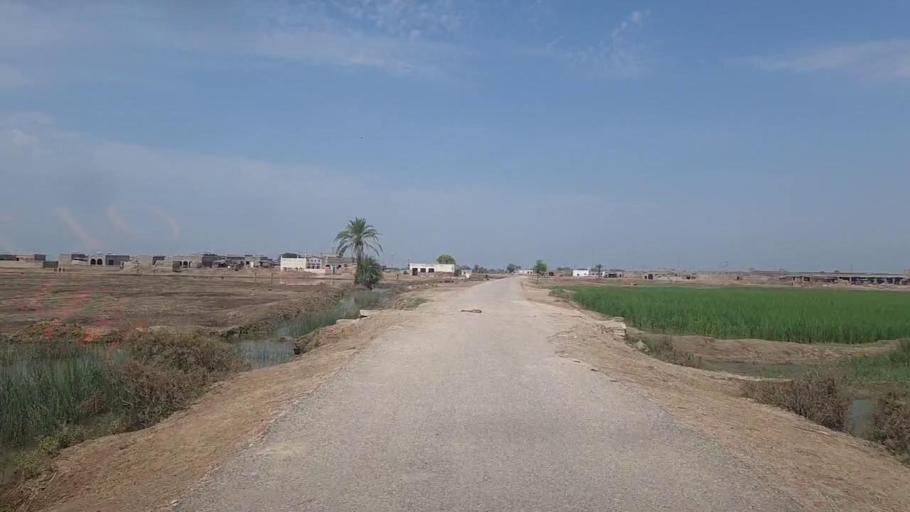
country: PK
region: Sindh
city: Thul
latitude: 28.2912
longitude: 68.6831
